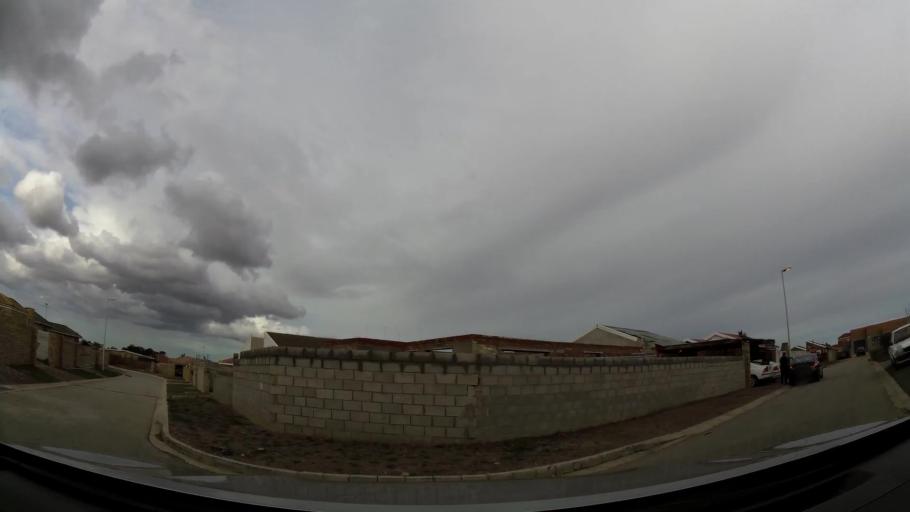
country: ZA
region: Eastern Cape
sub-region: Nelson Mandela Bay Metropolitan Municipality
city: Port Elizabeth
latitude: -33.9313
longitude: 25.5034
